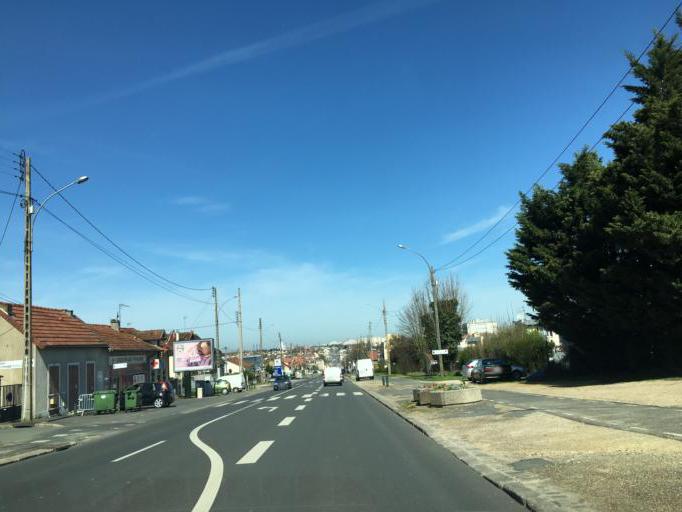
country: FR
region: Ile-de-France
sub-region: Departement de l'Essonne
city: Corbeil-Essonnes
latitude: 48.5943
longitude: 2.4762
